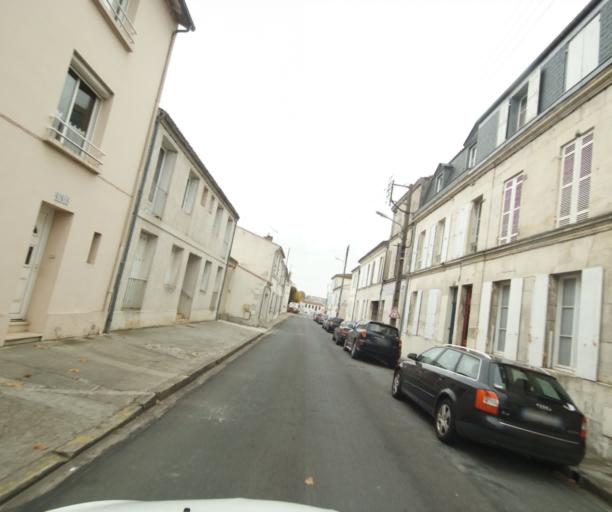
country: FR
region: Poitou-Charentes
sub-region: Departement de la Charente-Maritime
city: Saintes
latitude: 45.7472
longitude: -0.6225
